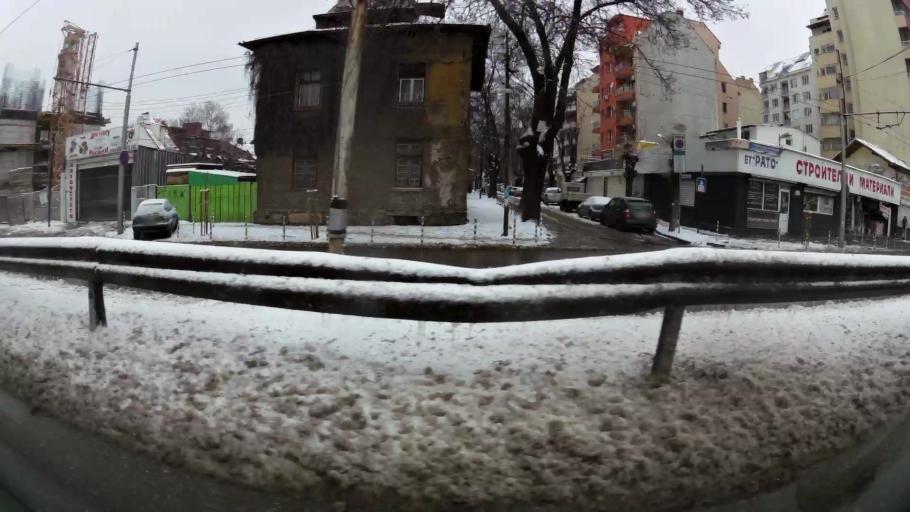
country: BG
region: Sofia-Capital
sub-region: Stolichna Obshtina
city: Sofia
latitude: 42.7067
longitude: 23.3322
